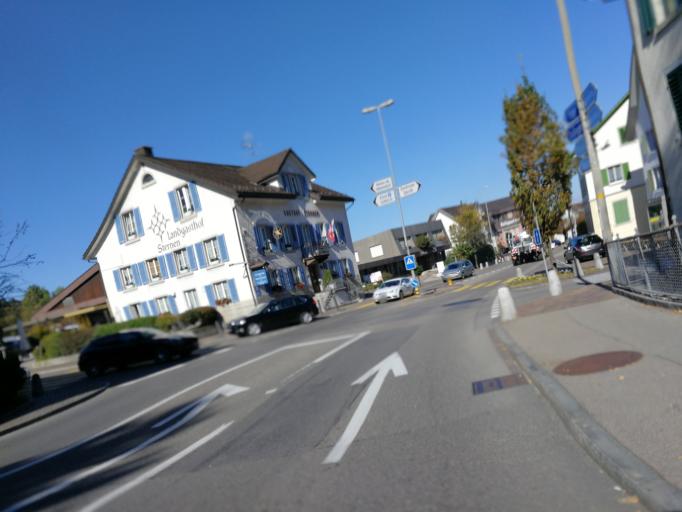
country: CH
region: Zurich
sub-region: Bezirk Meilen
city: Oetwil am See
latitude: 47.2707
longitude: 8.7202
